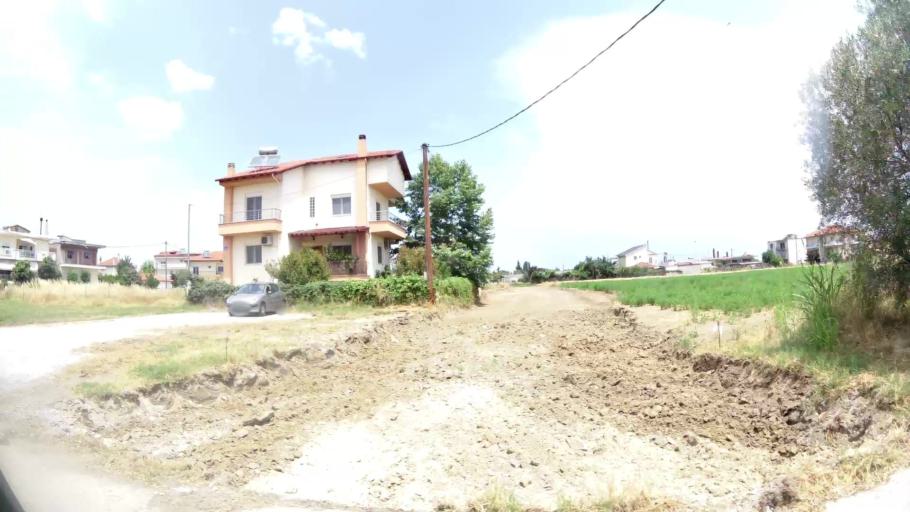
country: GR
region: Central Macedonia
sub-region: Nomos Pierias
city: Peristasi
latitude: 40.2713
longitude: 22.5454
